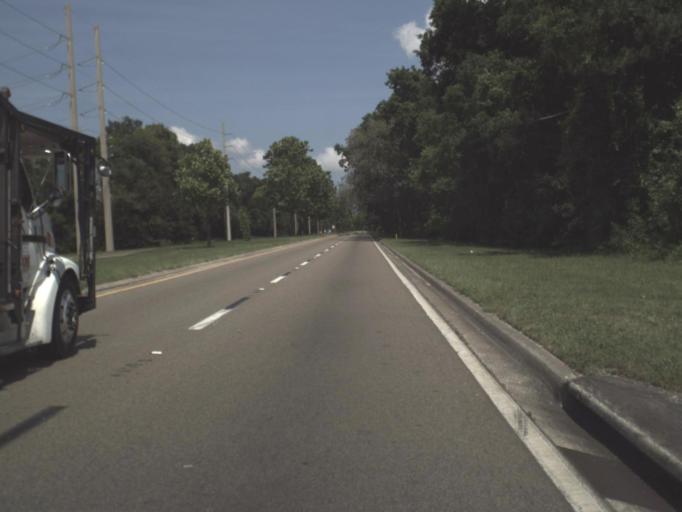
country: US
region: Florida
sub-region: Duval County
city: Jacksonville
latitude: 30.4073
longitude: -81.6360
